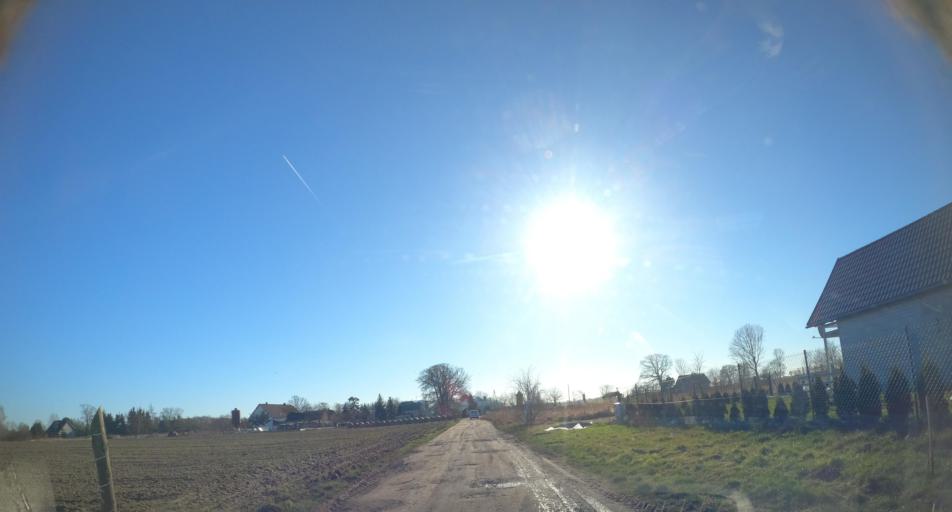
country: PL
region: West Pomeranian Voivodeship
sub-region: Powiat kamienski
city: Dziwnow
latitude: 54.0321
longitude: 14.8357
